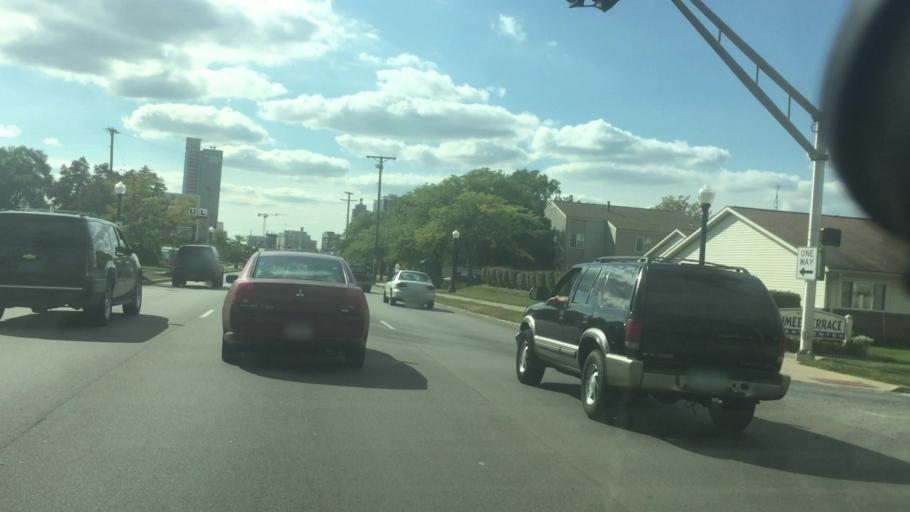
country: US
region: Indiana
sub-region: Allen County
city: Fort Wayne
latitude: 41.0789
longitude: -85.1260
